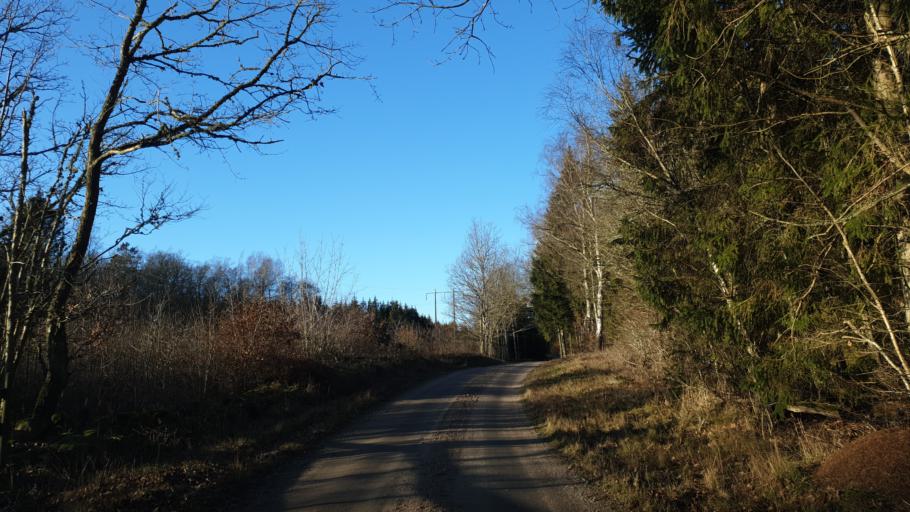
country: SE
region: Blekinge
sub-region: Karlskrona Kommun
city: Nattraby
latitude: 56.2592
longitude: 15.4145
